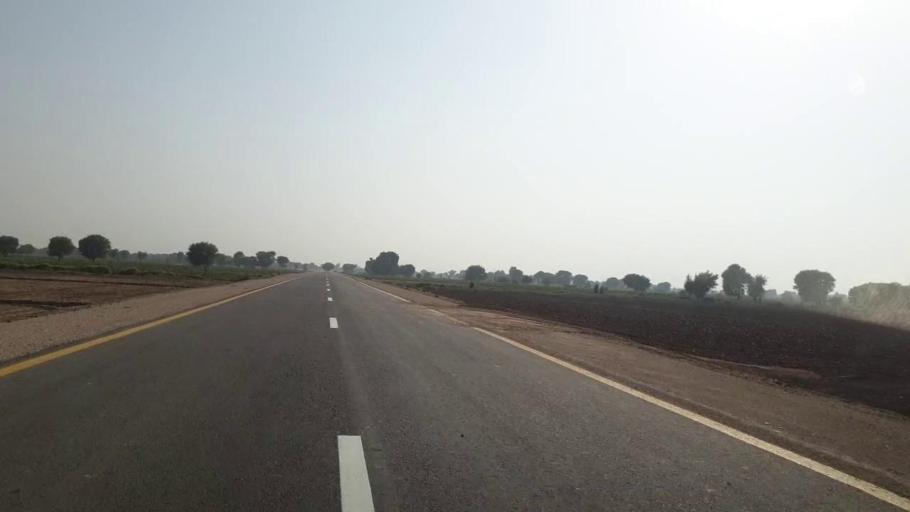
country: PK
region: Sindh
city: Bhan
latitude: 26.5134
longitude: 67.7855
